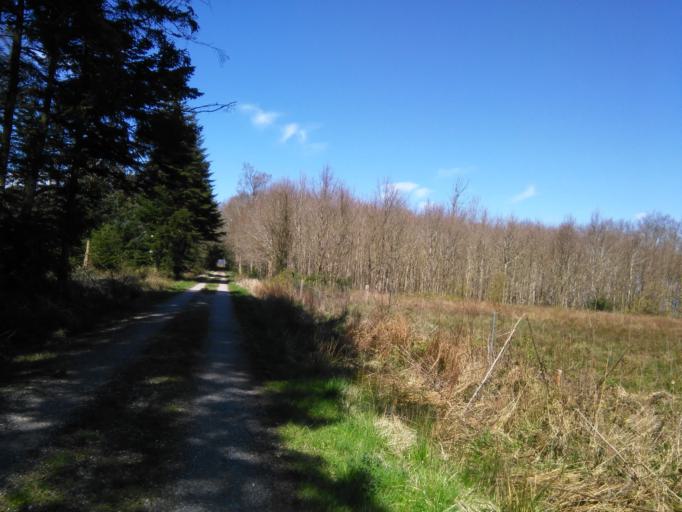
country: DK
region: Central Jutland
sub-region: Hedensted Kommune
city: Juelsminde
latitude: 55.7489
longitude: 10.0780
